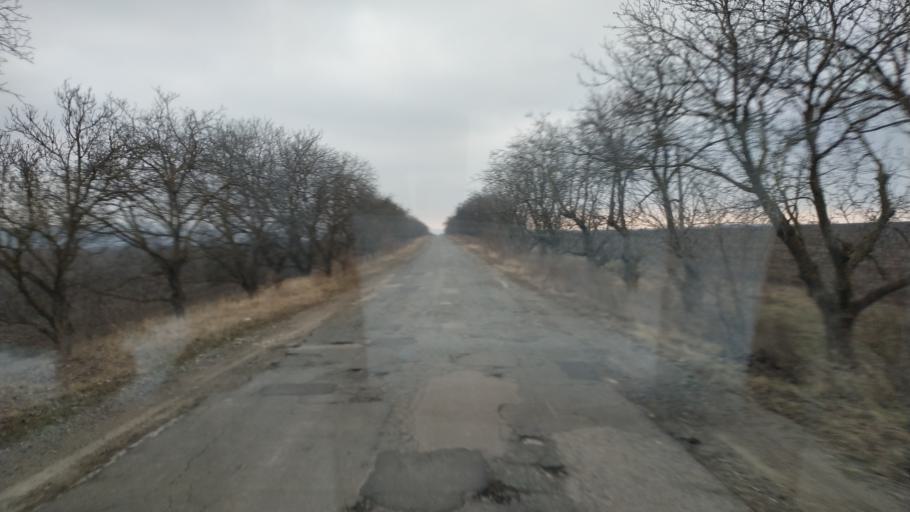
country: MD
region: Hincesti
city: Dancu
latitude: 46.8826
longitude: 28.2991
